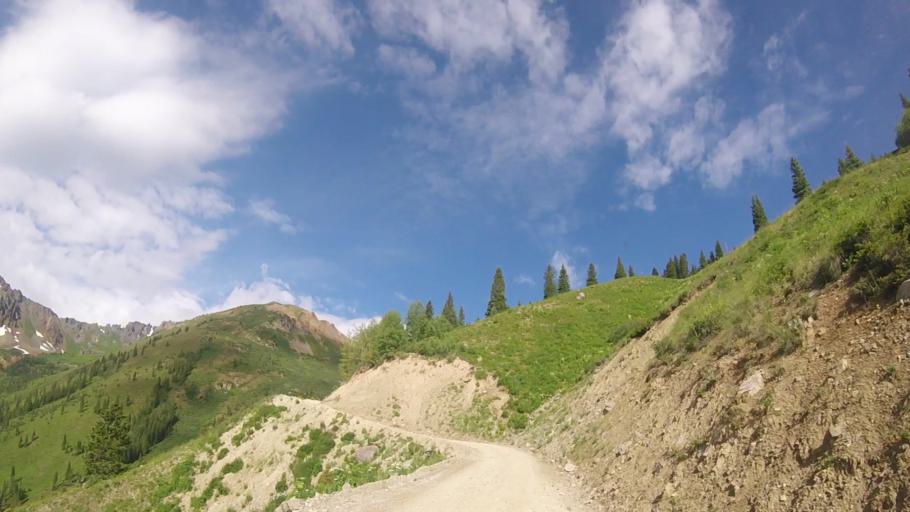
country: US
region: Colorado
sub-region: San Miguel County
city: Telluride
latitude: 37.8459
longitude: -107.7633
